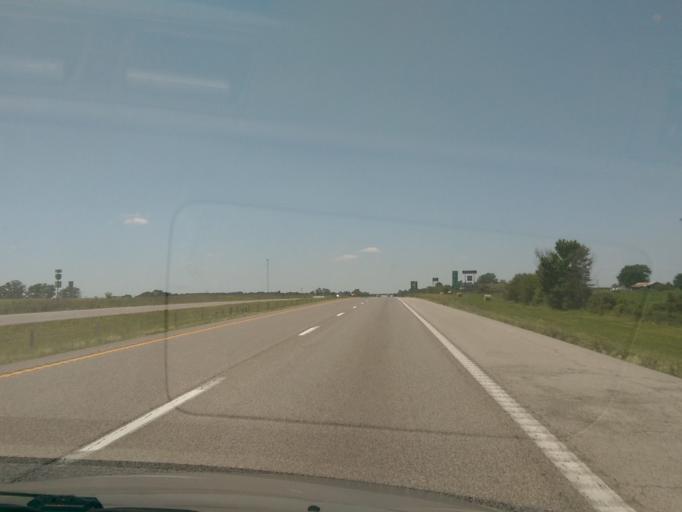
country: US
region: Missouri
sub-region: Saline County
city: Marshall
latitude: 38.9528
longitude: -93.0810
